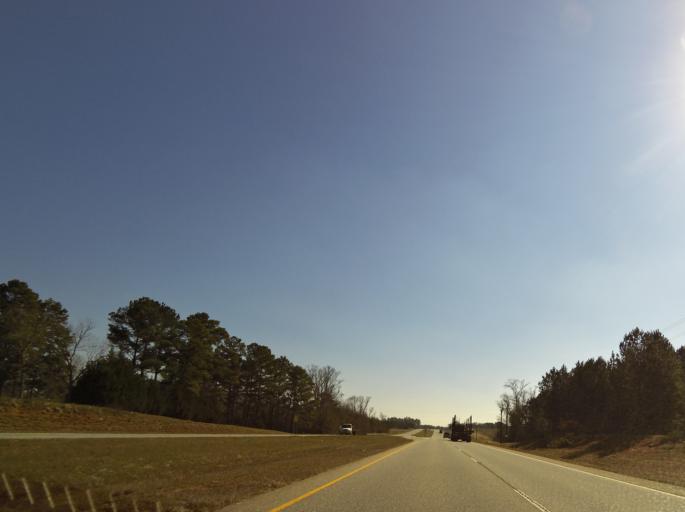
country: US
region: Georgia
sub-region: Pulaski County
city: Hawkinsville
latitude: 32.3118
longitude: -83.5193
